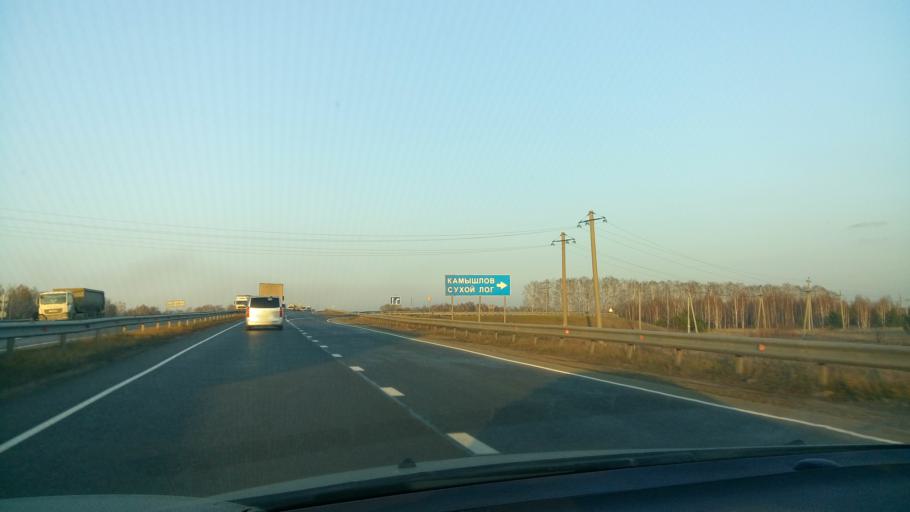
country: RU
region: Sverdlovsk
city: Yelanskiy
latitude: 56.8080
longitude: 62.5256
